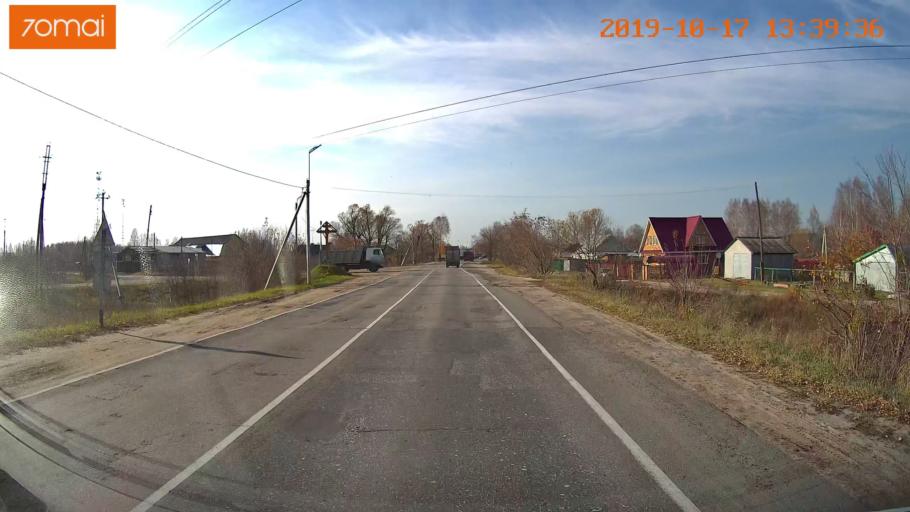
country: RU
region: Rjazan
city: Tuma
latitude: 55.1461
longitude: 40.5847
